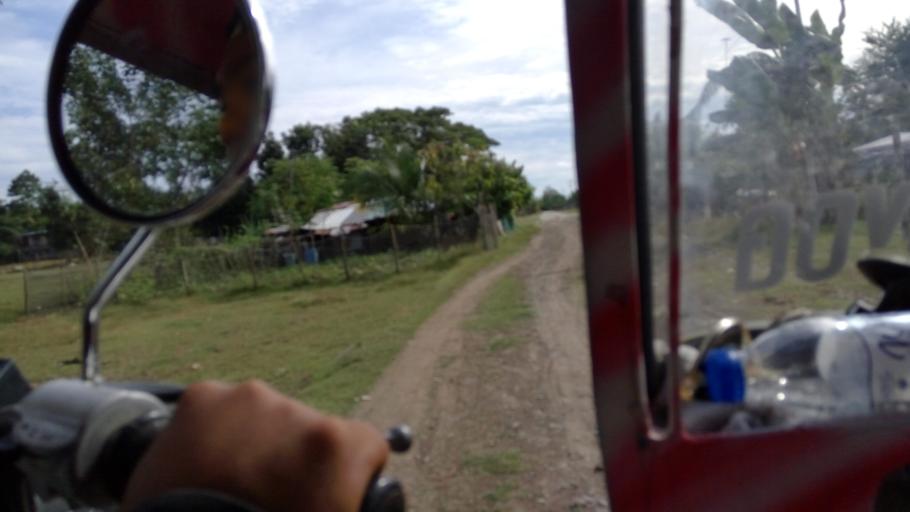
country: PH
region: Ilocos
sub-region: Province of La Union
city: Aringay
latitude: 16.3767
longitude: 120.3522
